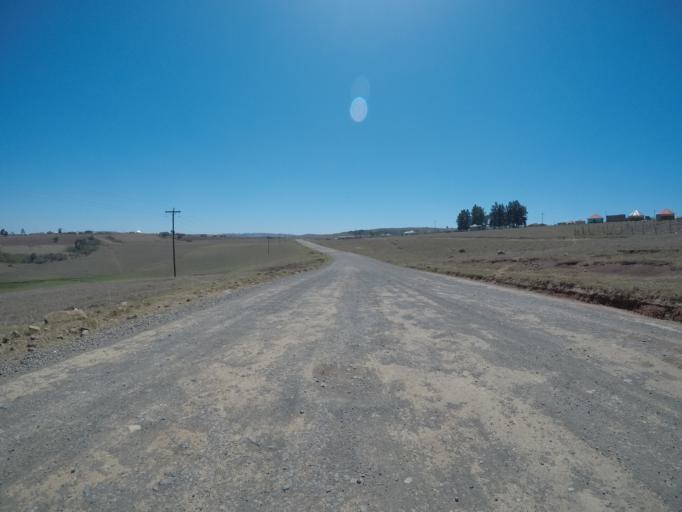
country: ZA
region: Eastern Cape
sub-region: OR Tambo District Municipality
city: Mthatha
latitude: -31.7856
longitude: 28.8109
